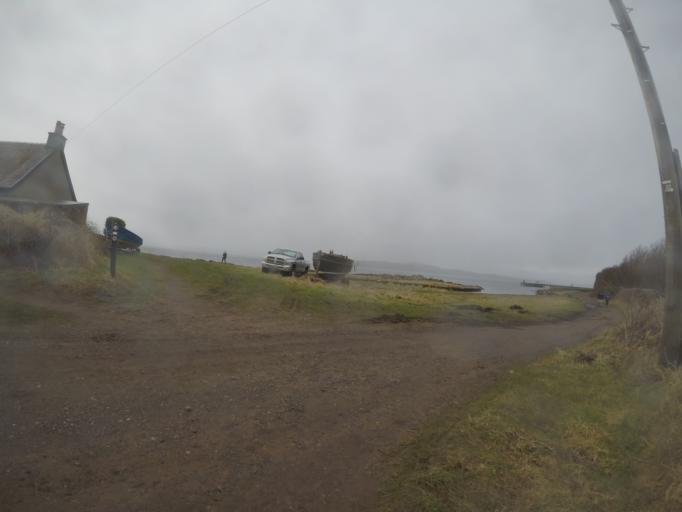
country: GB
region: Scotland
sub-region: North Ayrshire
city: West Kilbride
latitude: 55.7002
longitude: -4.9039
